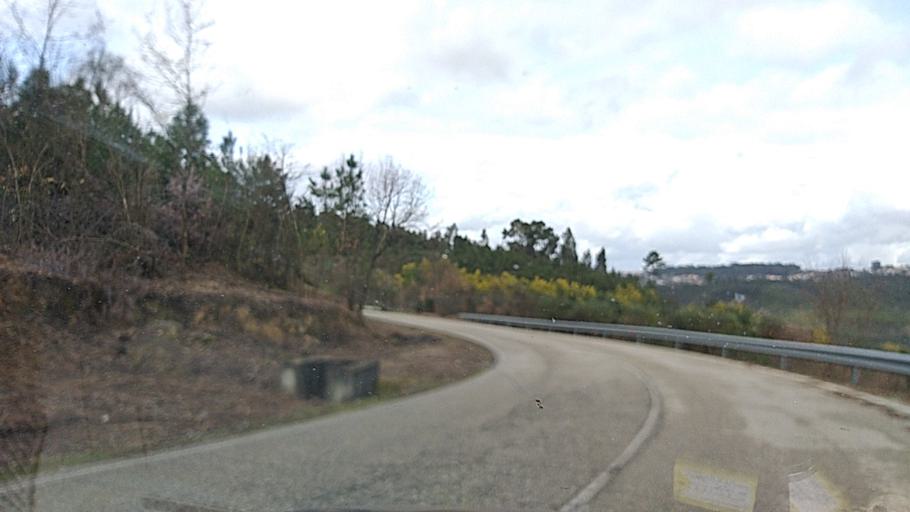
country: PT
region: Viseu
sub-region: Satao
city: Satao
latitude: 40.6616
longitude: -7.6655
